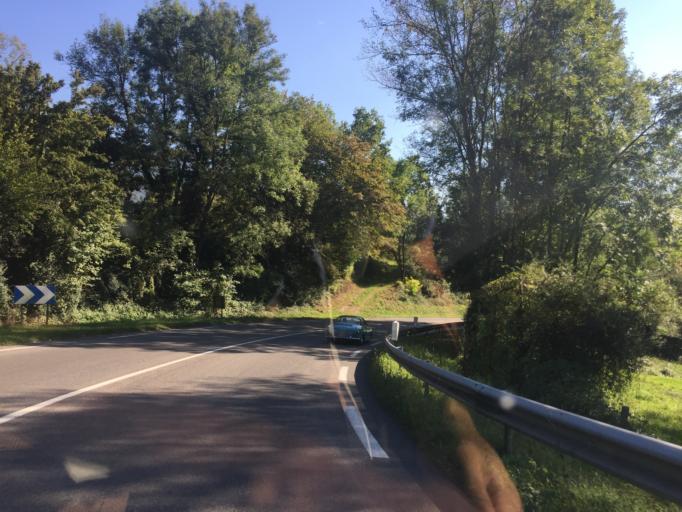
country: FR
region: Rhone-Alpes
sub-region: Departement de la Haute-Savoie
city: Viuz-la-Chiesaz
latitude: 45.8390
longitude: 6.0595
